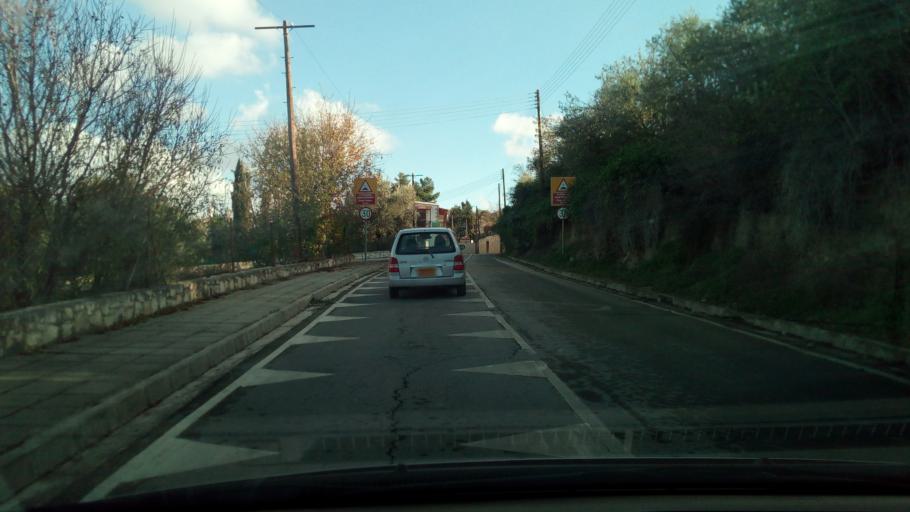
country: CY
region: Pafos
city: Polis
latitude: 34.9426
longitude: 32.5031
